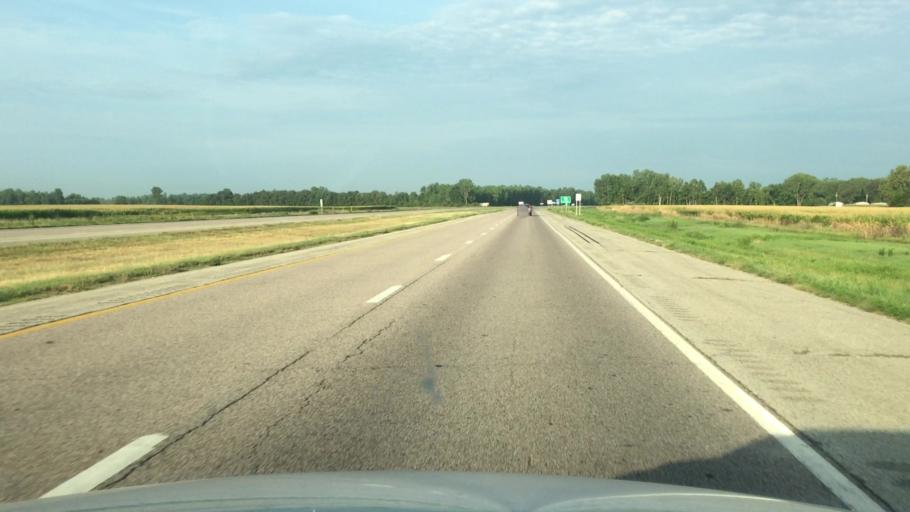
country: US
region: Kansas
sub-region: Doniphan County
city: Elwood
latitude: 39.7477
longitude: -94.8752
